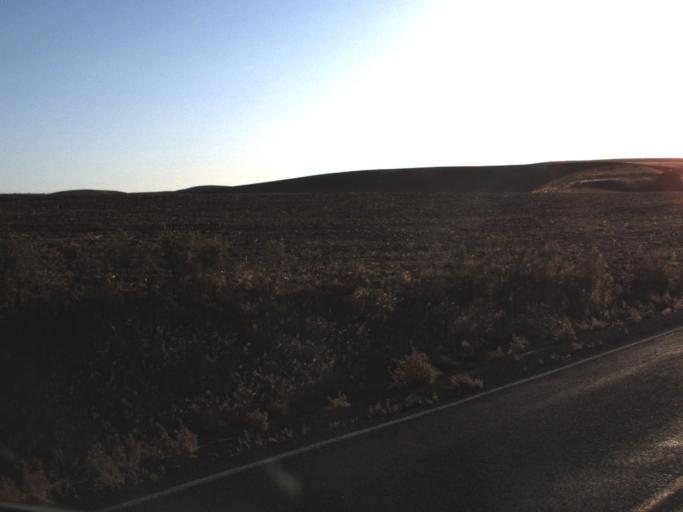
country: US
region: Washington
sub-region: Adams County
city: Ritzville
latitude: 46.6771
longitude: -118.3625
